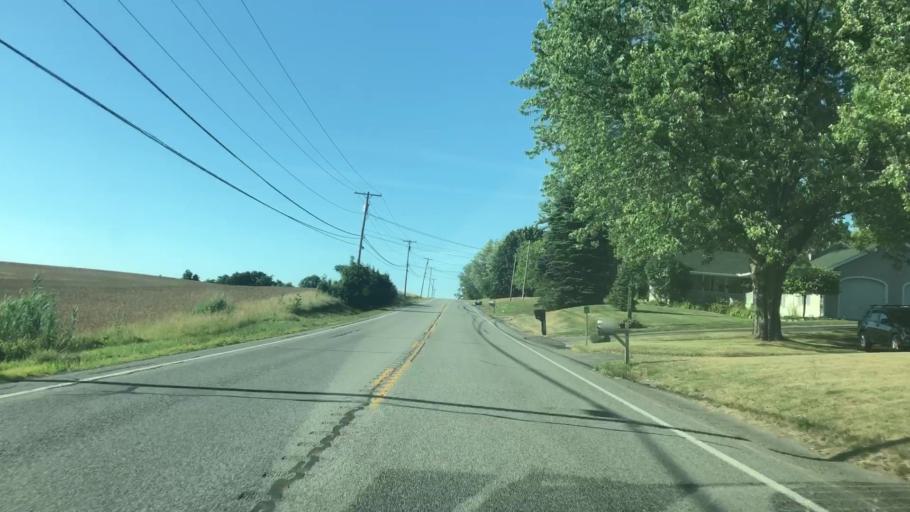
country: US
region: New York
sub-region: Wayne County
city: Macedon
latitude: 43.1342
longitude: -77.2926
